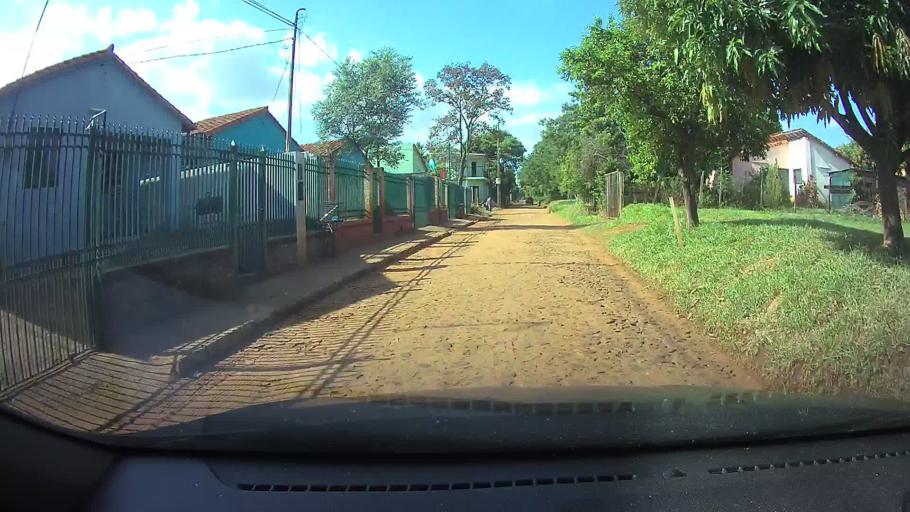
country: PY
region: Central
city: Limpio
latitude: -25.2463
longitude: -57.4678
